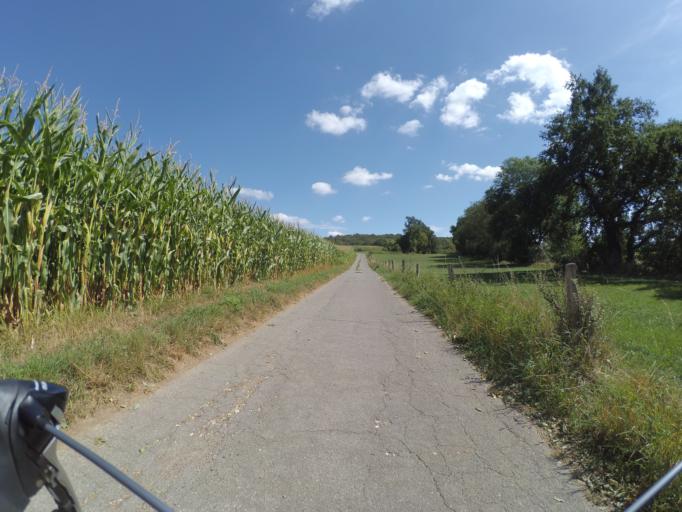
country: NL
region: Limburg
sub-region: Gemeente Simpelveld
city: Simpelveld
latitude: 50.7995
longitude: 5.9794
